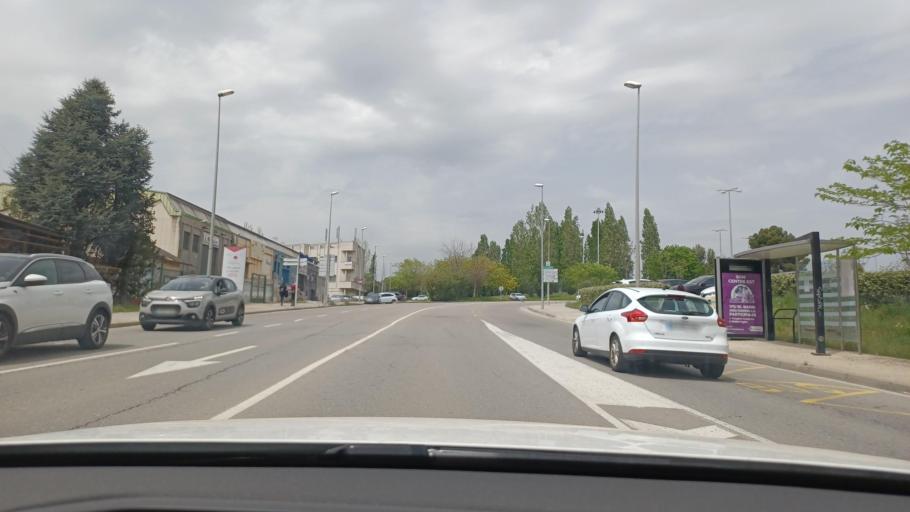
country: ES
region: Catalonia
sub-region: Provincia de Barcelona
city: Sant Cugat del Valles
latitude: 41.4792
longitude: 2.0939
